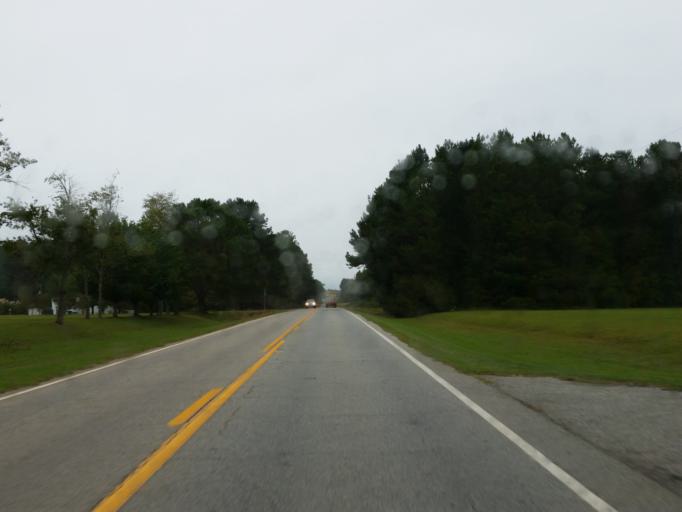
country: US
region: Georgia
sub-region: Berrien County
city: Ray City
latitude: 31.1122
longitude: -83.2988
